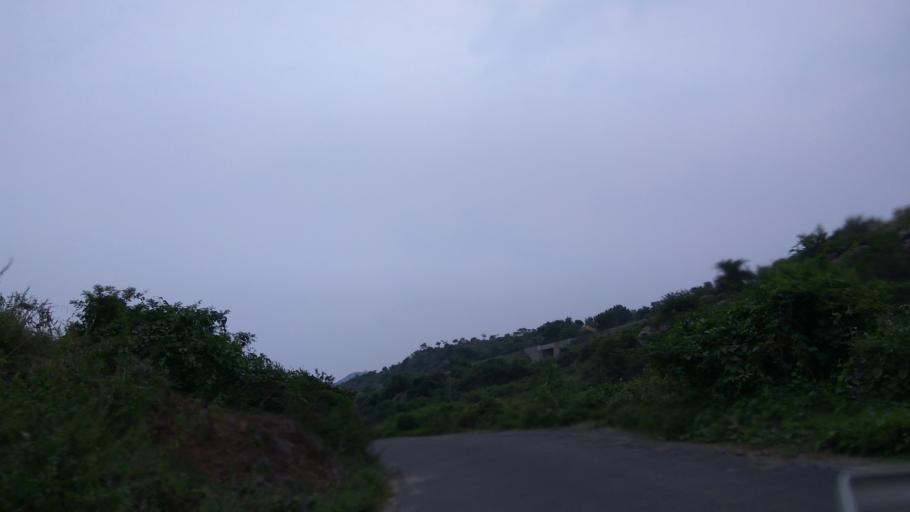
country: IN
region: Tamil Nadu
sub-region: Dharmapuri
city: Dharmapuri
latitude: 12.0212
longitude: 78.1192
